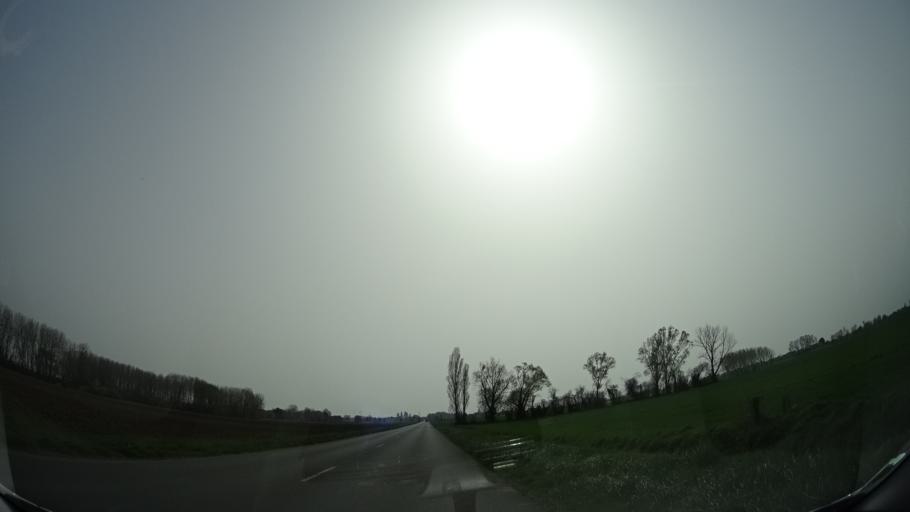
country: FR
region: Pays de la Loire
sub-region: Departement de Maine-et-Loire
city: Doue-la-Fontaine
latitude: 47.2056
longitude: -0.2915
